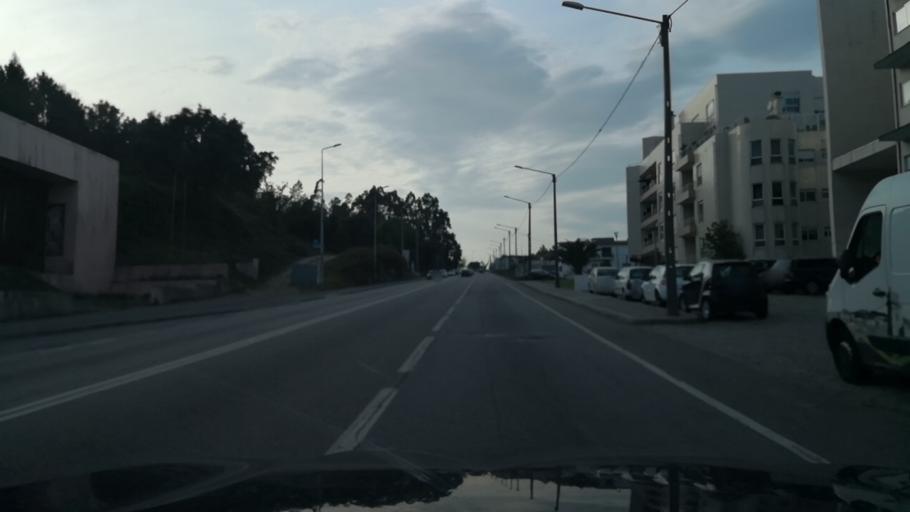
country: PT
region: Porto
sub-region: Valongo
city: Valongo
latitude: 41.1918
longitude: -8.5136
